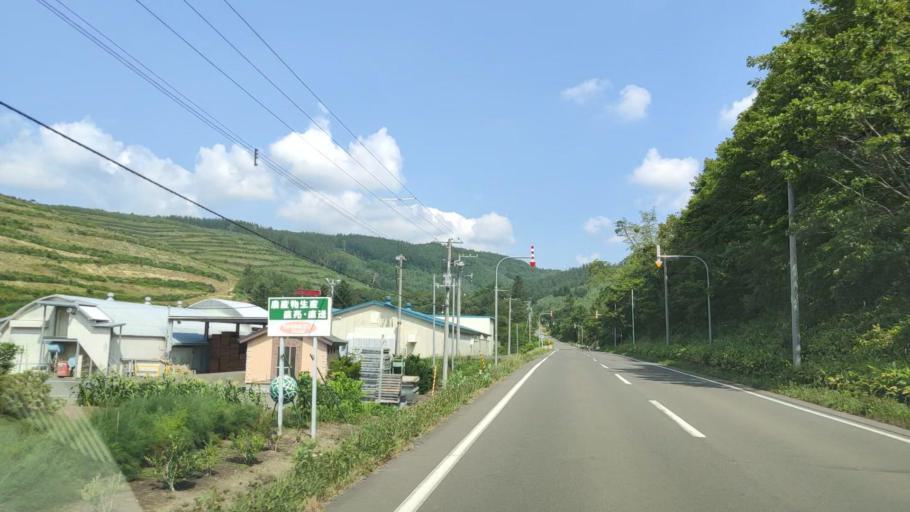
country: JP
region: Hokkaido
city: Shimo-furano
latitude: 43.4215
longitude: 142.4014
